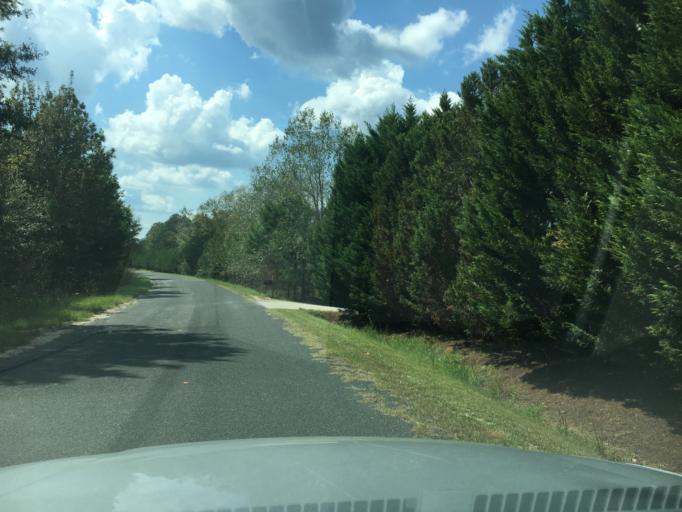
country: US
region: South Carolina
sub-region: Greenwood County
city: Greenwood
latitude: 34.0623
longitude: -82.1508
